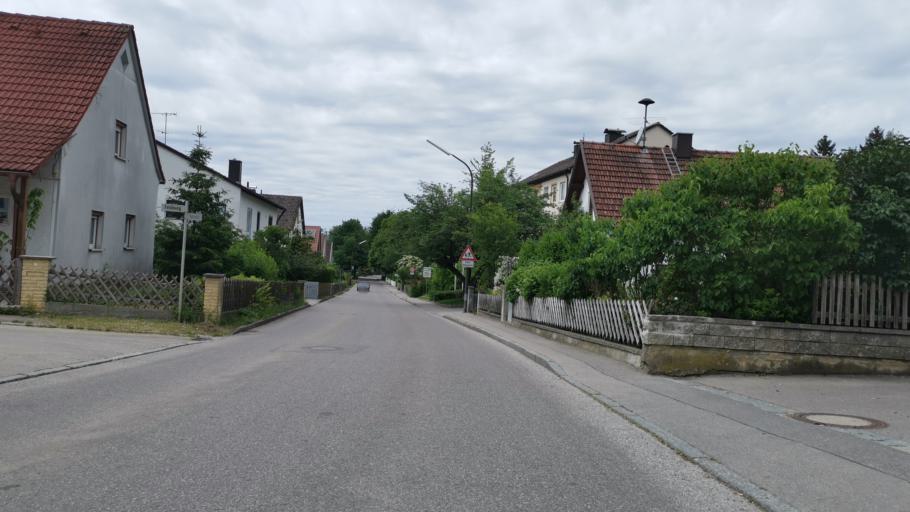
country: DE
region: Bavaria
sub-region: Upper Bavaria
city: Hattenhofen
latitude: 48.2224
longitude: 11.1160
